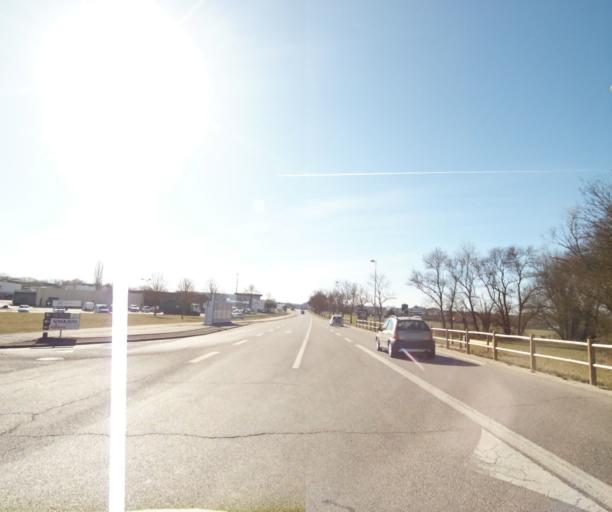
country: FR
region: Lorraine
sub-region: Departement de Meurthe-et-Moselle
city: Ludres
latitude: 48.6251
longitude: 6.1785
